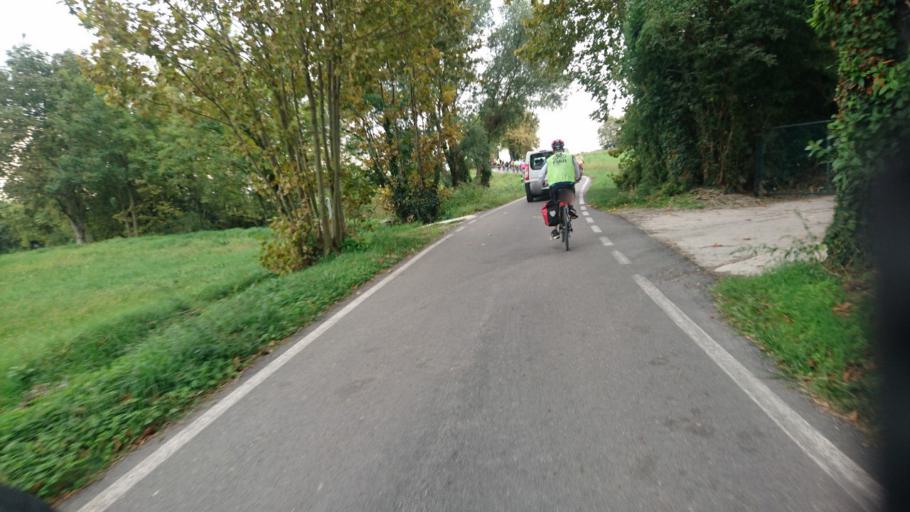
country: IT
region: Veneto
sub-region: Provincia di Verona
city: San Martino Buon Albergo
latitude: 45.4075
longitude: 11.1075
